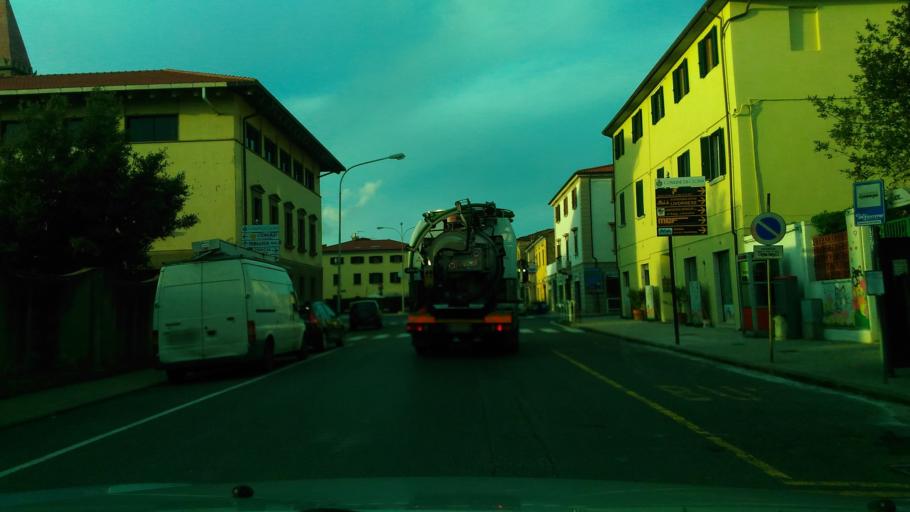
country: IT
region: Tuscany
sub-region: Provincia di Livorno
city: S.P. in Palazzi
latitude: 43.3265
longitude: 10.5078
